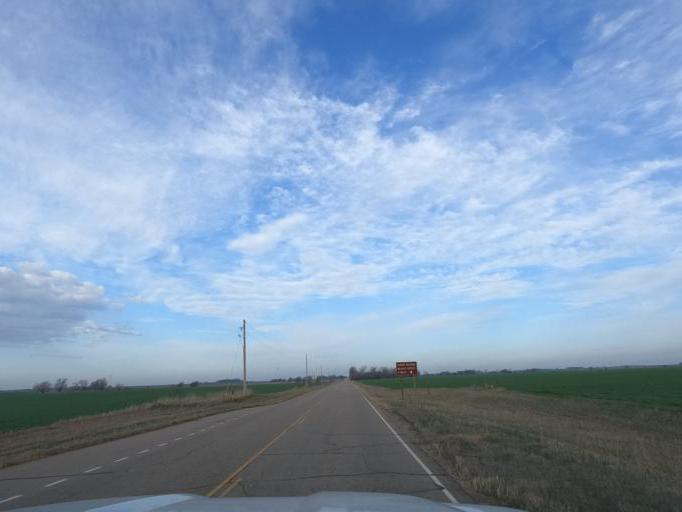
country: US
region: Kansas
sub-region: Reno County
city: Nickerson
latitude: 38.0577
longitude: -98.1808
